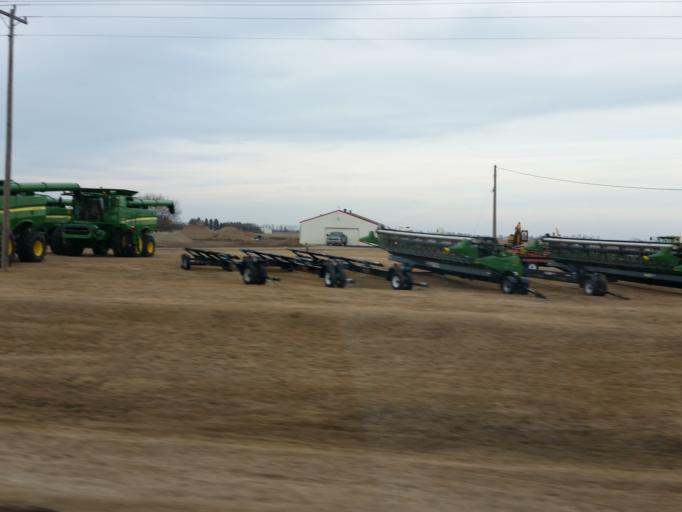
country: US
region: North Dakota
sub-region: Traill County
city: Hillsboro
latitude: 47.1858
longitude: -97.2174
